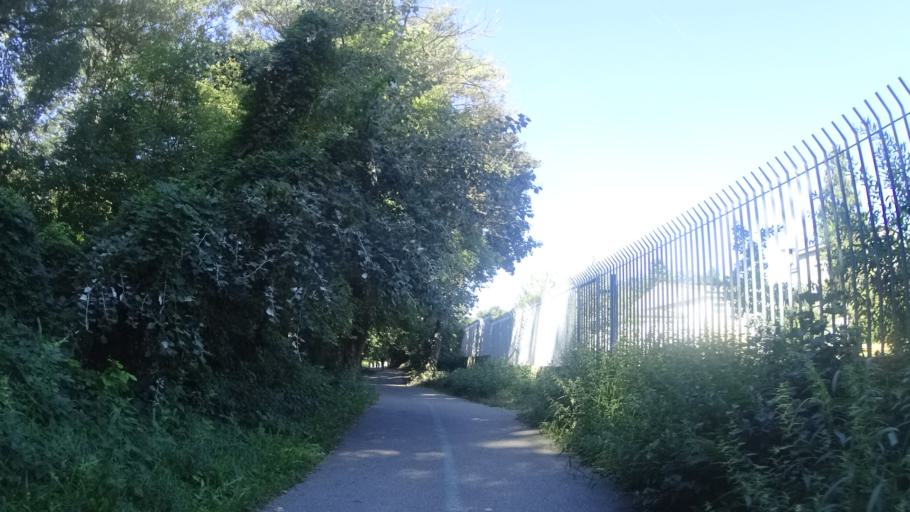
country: SK
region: Bratislavsky
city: Bratislava
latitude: 48.1468
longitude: 17.0635
